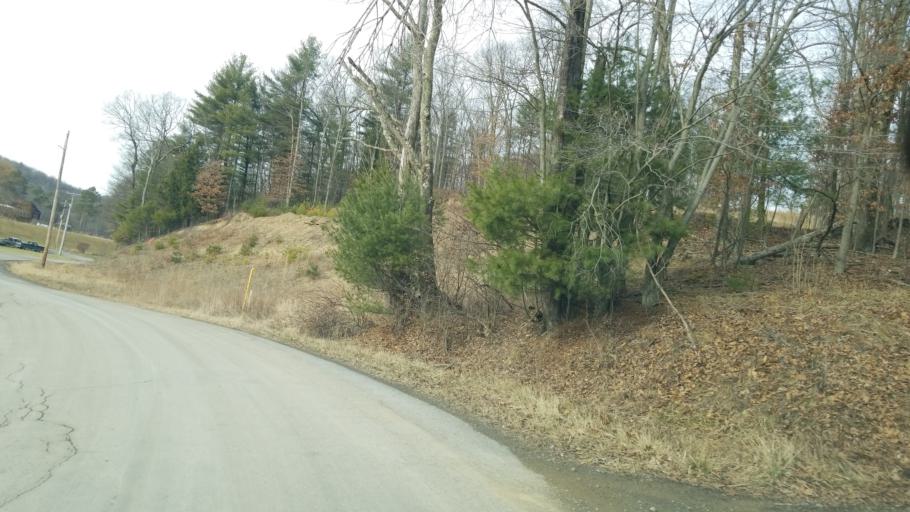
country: US
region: Pennsylvania
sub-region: Jefferson County
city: Punxsutawney
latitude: 40.8485
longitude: -79.0014
